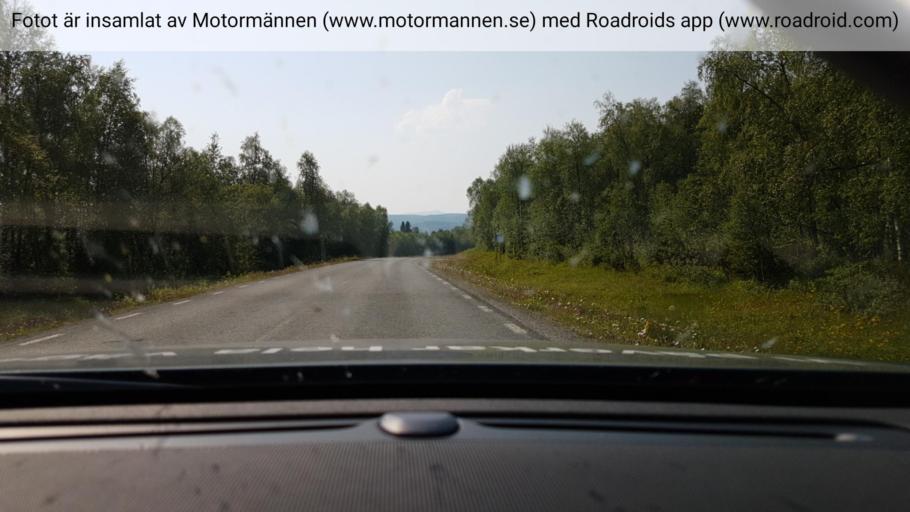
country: NO
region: Nordland
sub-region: Rana
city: Mo i Rana
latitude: 65.7594
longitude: 15.1157
